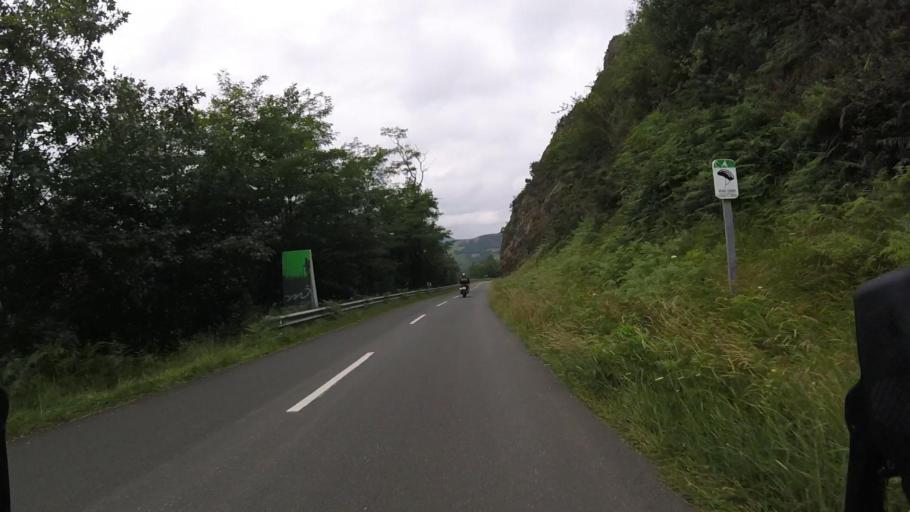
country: ES
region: Basque Country
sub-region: Provincia de Guipuzcoa
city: Irun
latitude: 43.2728
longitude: -1.7977
